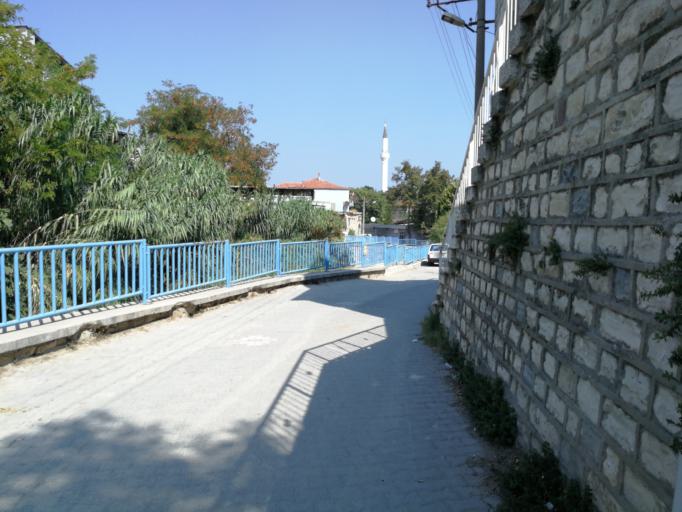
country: TR
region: Izmir
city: Urla
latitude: 38.3208
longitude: 26.7669
